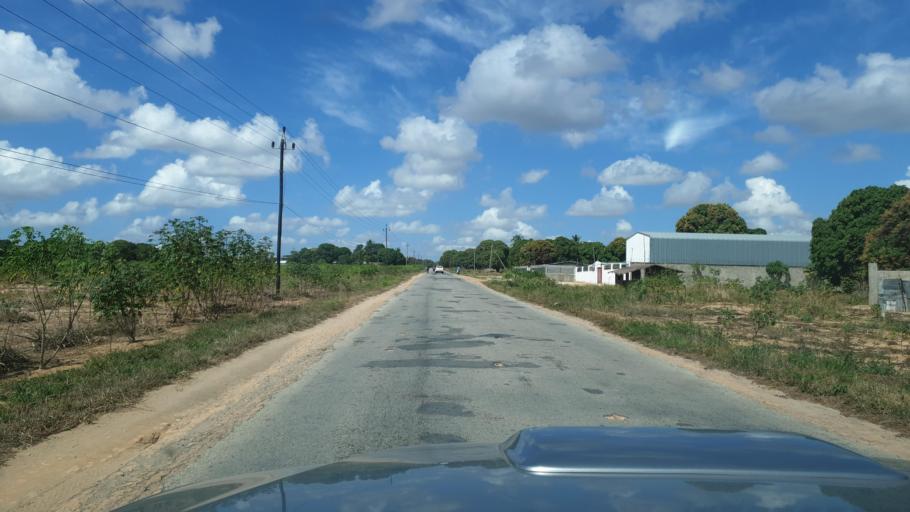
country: MZ
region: Nampula
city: Nacala
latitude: -14.4990
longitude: 40.6964
